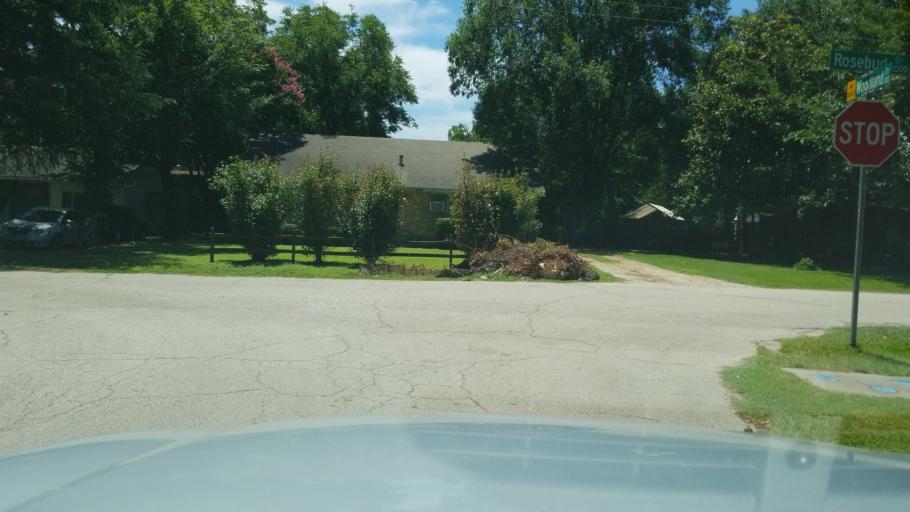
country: US
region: Texas
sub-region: Dallas County
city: Irving
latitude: 32.8042
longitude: -96.9122
